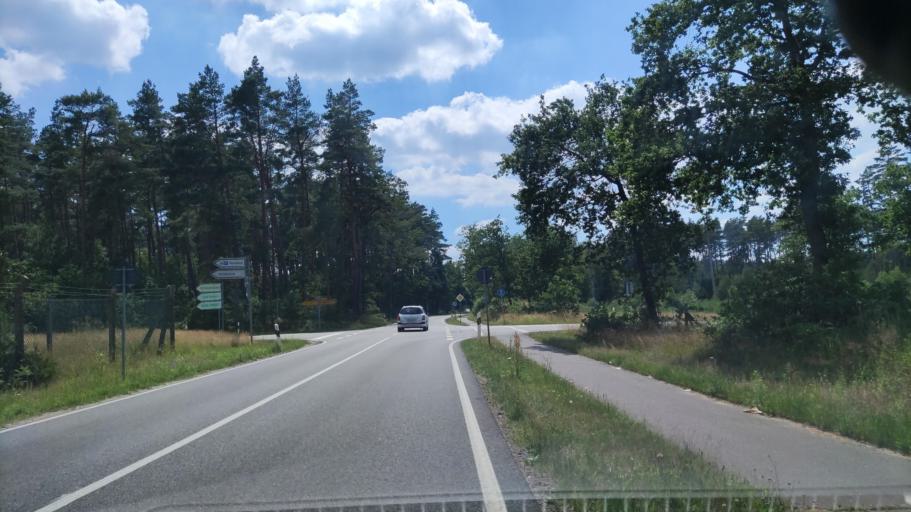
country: DE
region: Mecklenburg-Vorpommern
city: Lubtheen
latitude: 53.3197
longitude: 11.1009
